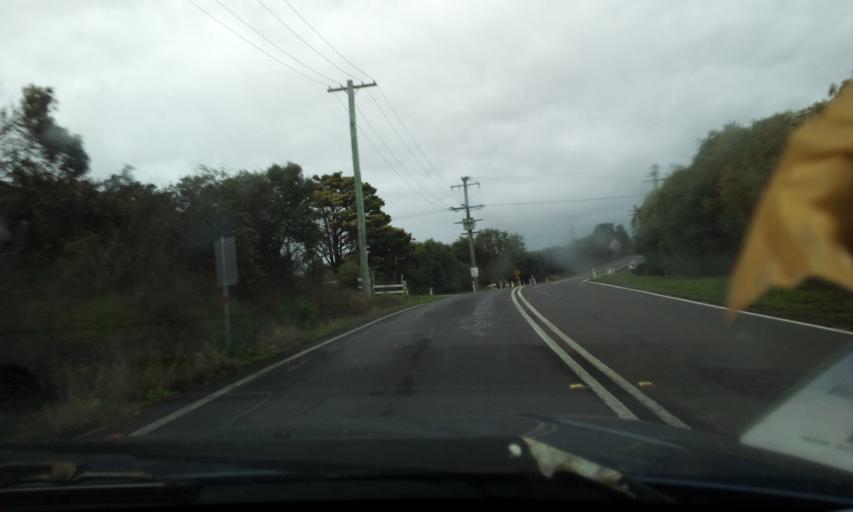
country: AU
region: New South Wales
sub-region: Wollondilly
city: Douglas Park
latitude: -34.1646
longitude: 150.7152
